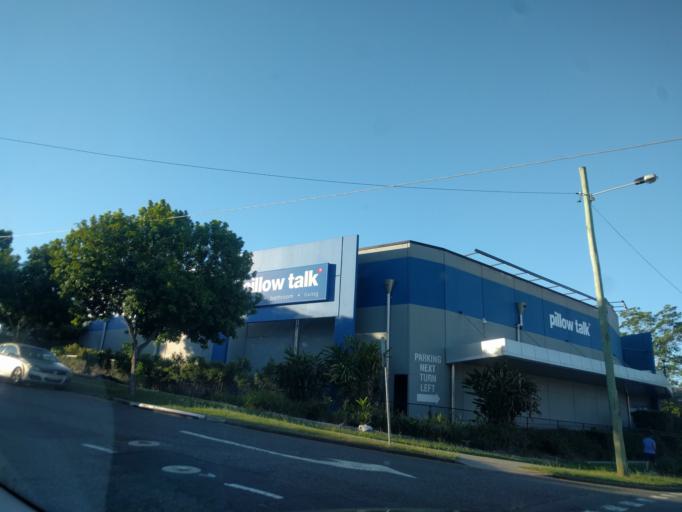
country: AU
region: Queensland
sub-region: Brisbane
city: Annerley
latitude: -27.5024
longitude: 153.0344
